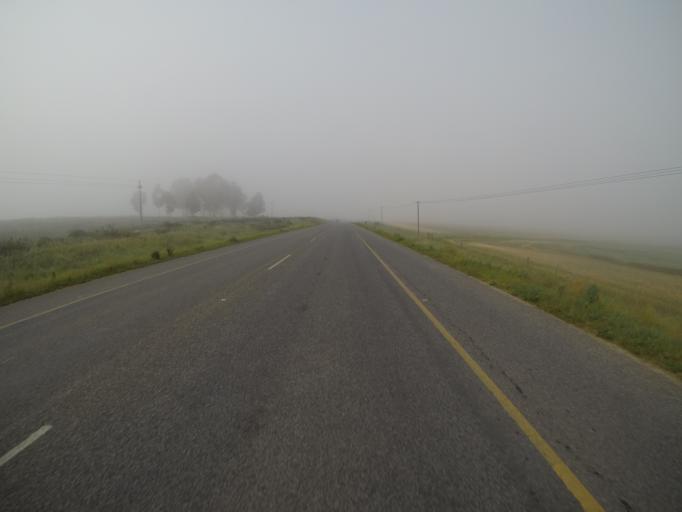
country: ZA
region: Western Cape
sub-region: City of Cape Town
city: Kraaifontein
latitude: -33.6841
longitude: 18.7052
